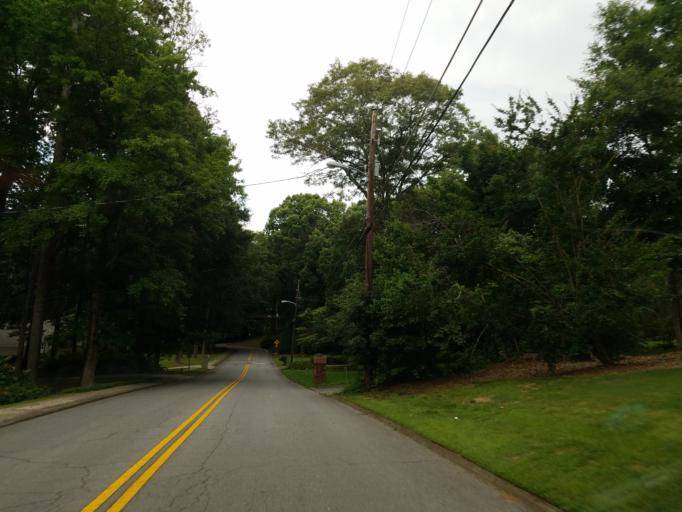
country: US
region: Georgia
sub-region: Cobb County
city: Marietta
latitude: 33.9323
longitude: -84.5708
